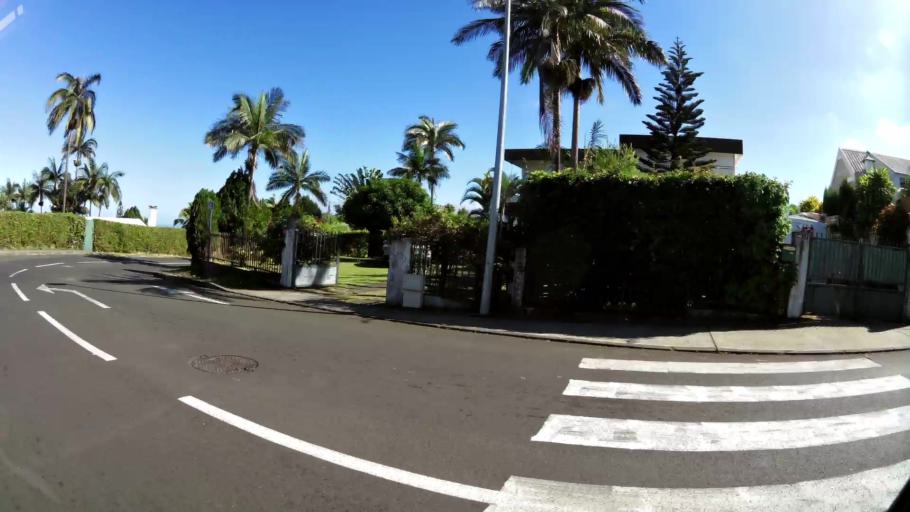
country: RE
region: Reunion
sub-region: Reunion
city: Le Tampon
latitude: -21.2732
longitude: 55.5144
